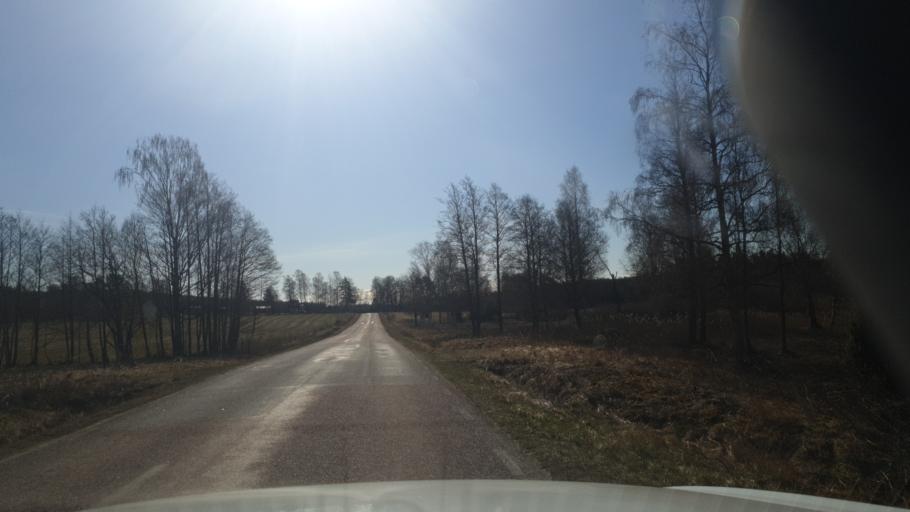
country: SE
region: Vaermland
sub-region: Arvika Kommun
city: Arvika
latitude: 59.5377
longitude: 12.7969
